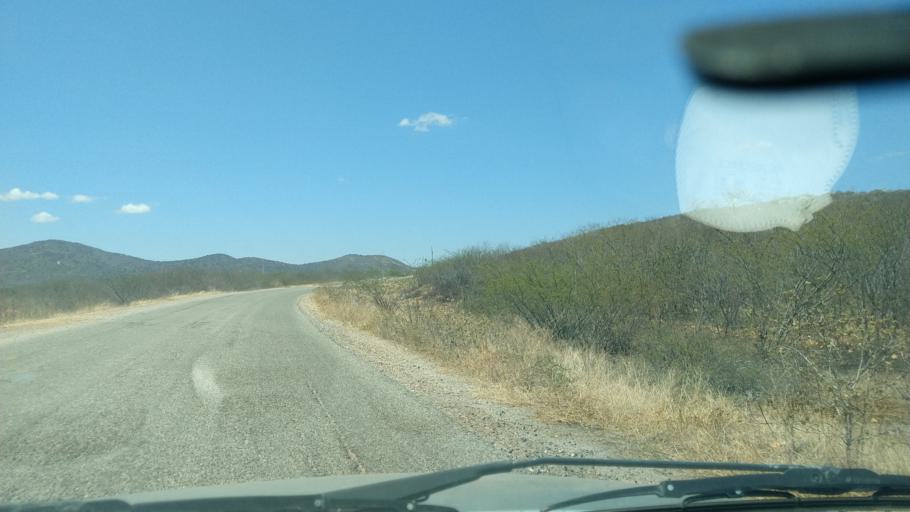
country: BR
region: Rio Grande do Norte
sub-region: Sao Tome
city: Sao Tome
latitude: -5.9729
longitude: -36.1362
